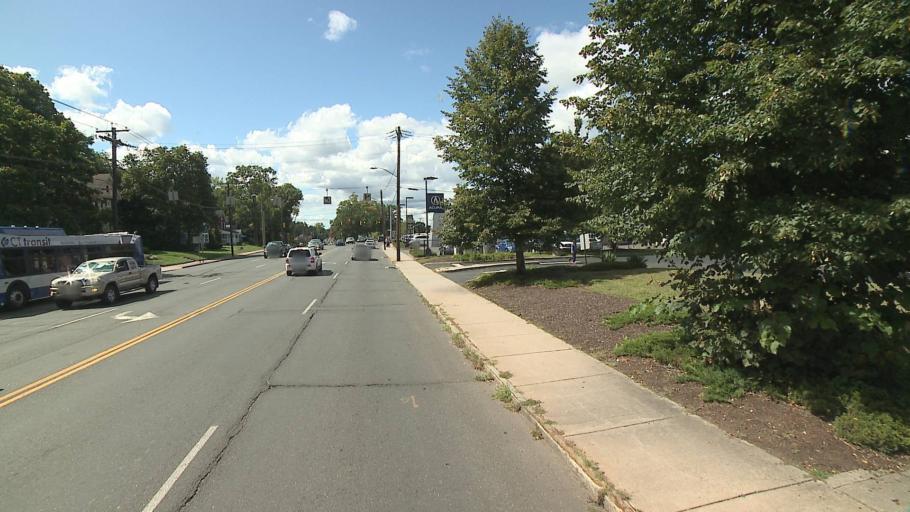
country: US
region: Connecticut
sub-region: Hartford County
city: Manchester
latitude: 41.7726
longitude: -72.5338
